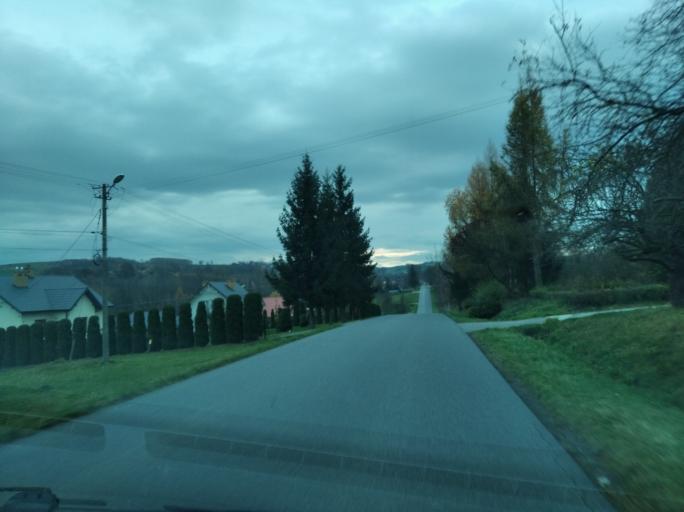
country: PL
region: Subcarpathian Voivodeship
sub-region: Powiat ropczycko-sedziszowski
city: Iwierzyce
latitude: 49.9974
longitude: 21.7423
